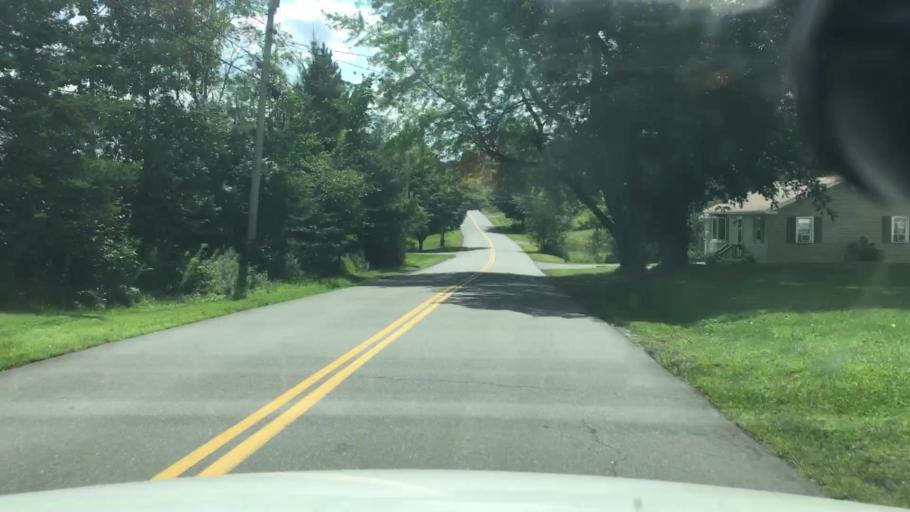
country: US
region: Maine
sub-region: Somerset County
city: Skowhegan
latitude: 44.7533
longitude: -69.7169
